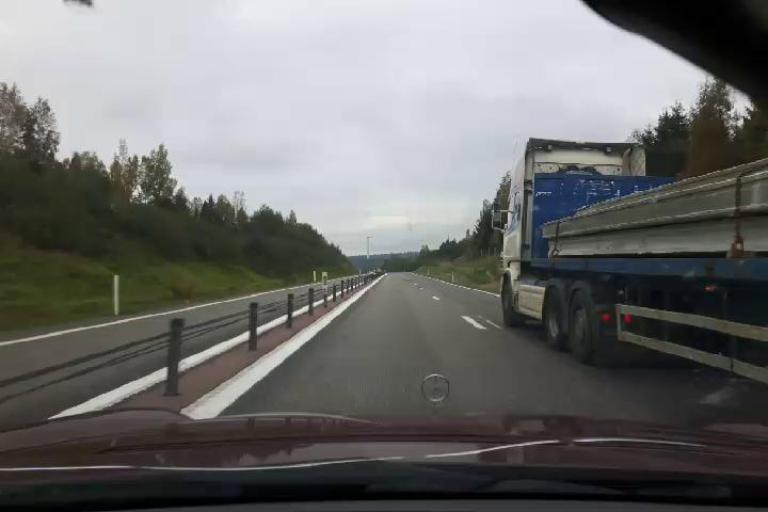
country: SE
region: Vaesternorrland
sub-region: Haernoesands Kommun
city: Haernoesand
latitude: 62.7647
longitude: 17.9078
